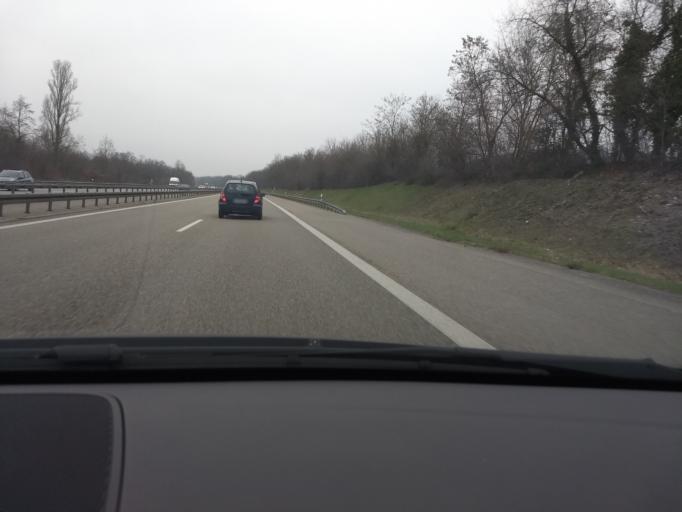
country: DE
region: Baden-Wuerttemberg
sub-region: Freiburg Region
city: Bad Bellingen
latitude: 47.7305
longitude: 7.5509
